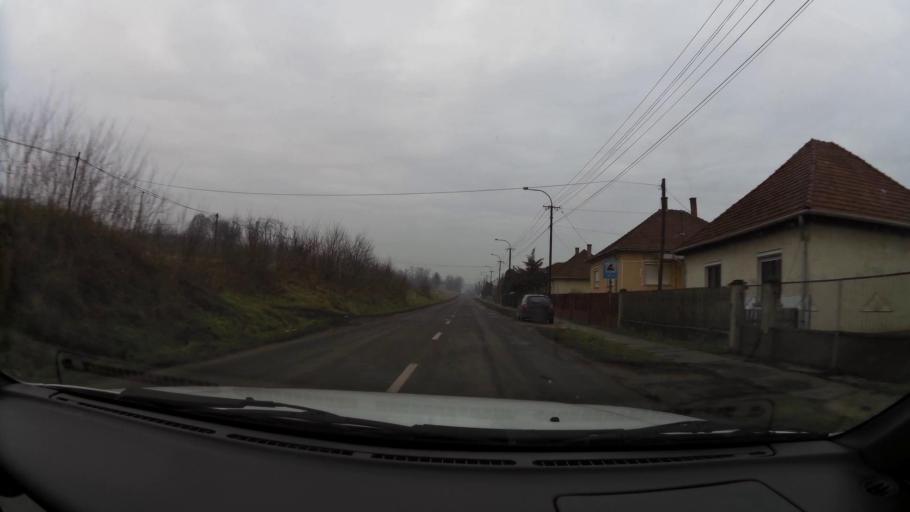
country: HU
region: Borsod-Abauj-Zemplen
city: Izsofalva
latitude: 48.3110
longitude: 20.6526
